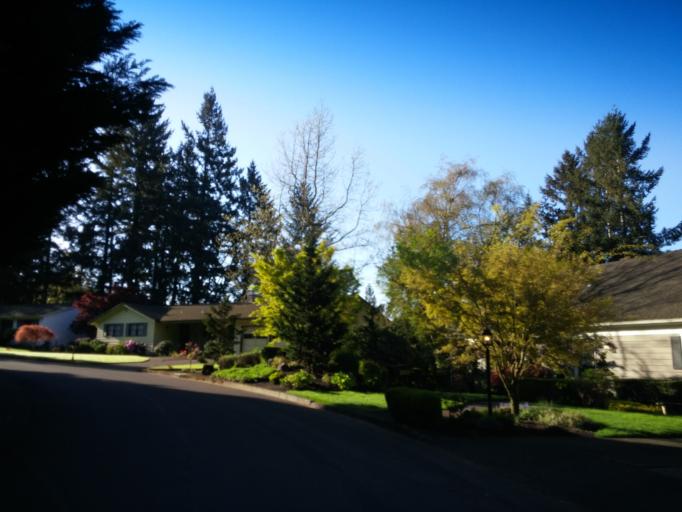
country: US
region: Oregon
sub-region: Washington County
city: Cedar Hills
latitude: 45.5103
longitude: -122.7929
